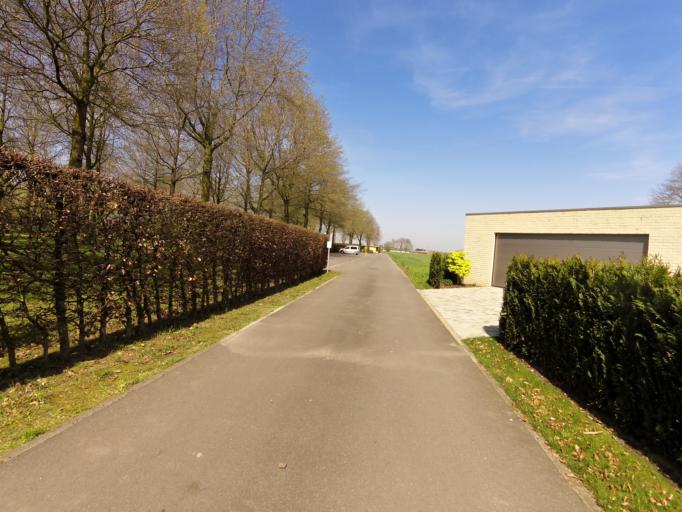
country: BE
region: Flanders
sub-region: Provincie West-Vlaanderen
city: Koekelare
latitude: 51.0921
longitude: 2.9852
